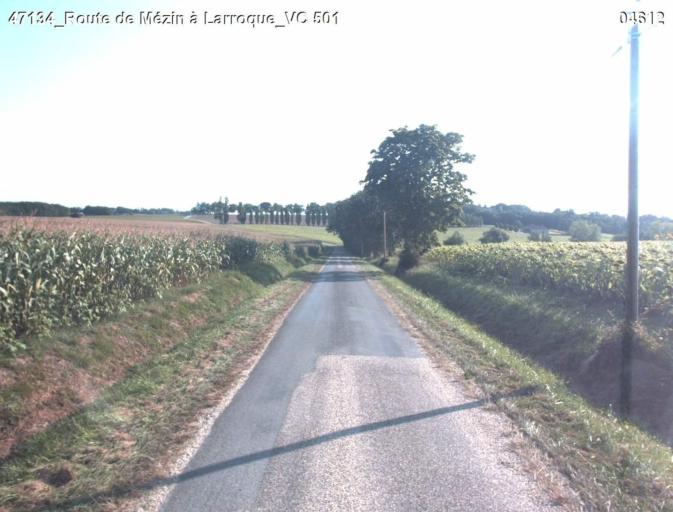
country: FR
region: Aquitaine
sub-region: Departement du Lot-et-Garonne
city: Mezin
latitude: 44.0357
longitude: 0.2685
